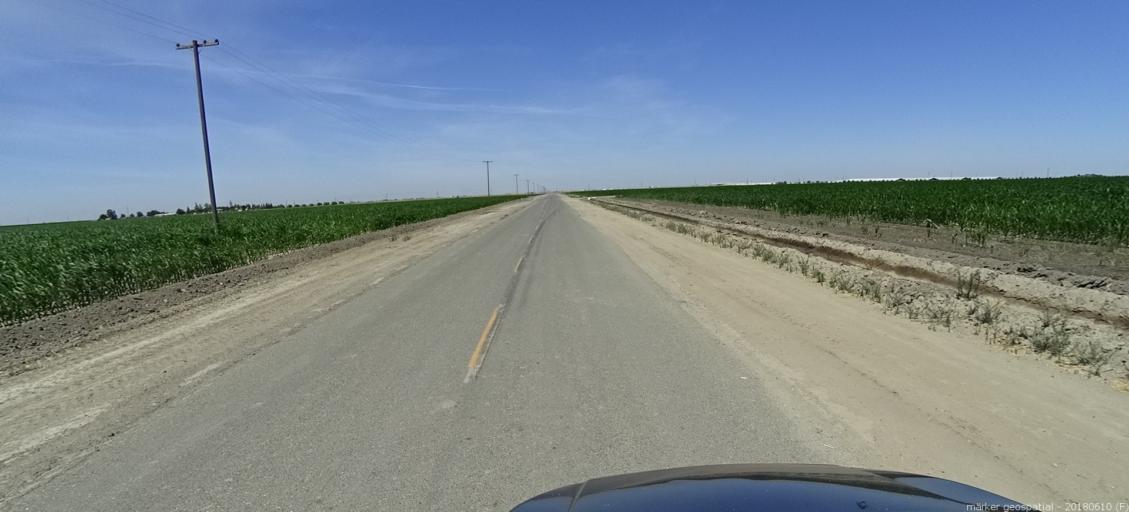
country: US
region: California
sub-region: Merced County
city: Dos Palos
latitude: 37.0546
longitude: -120.4615
